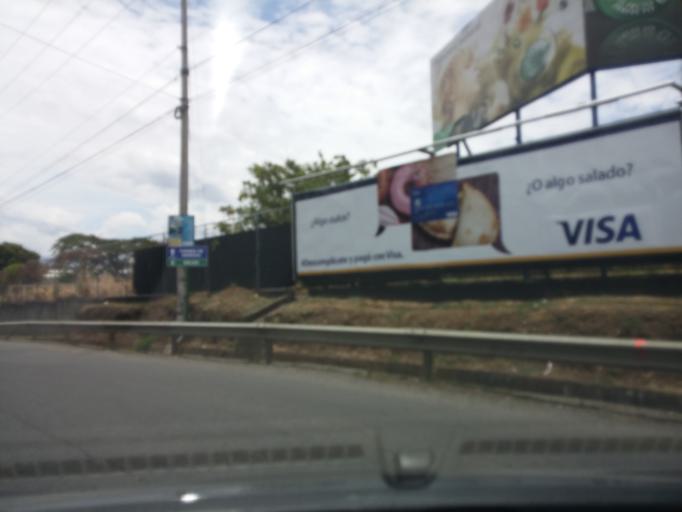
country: CR
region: Heredia
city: San Francisco
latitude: 9.9714
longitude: -84.1353
